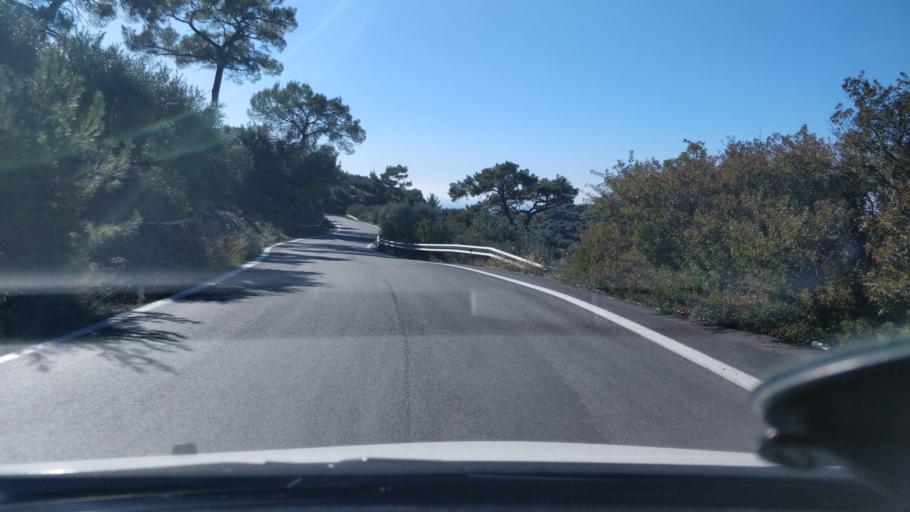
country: GR
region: Crete
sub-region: Nomos Irakleiou
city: Kastelli
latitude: 35.0157
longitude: 25.4479
